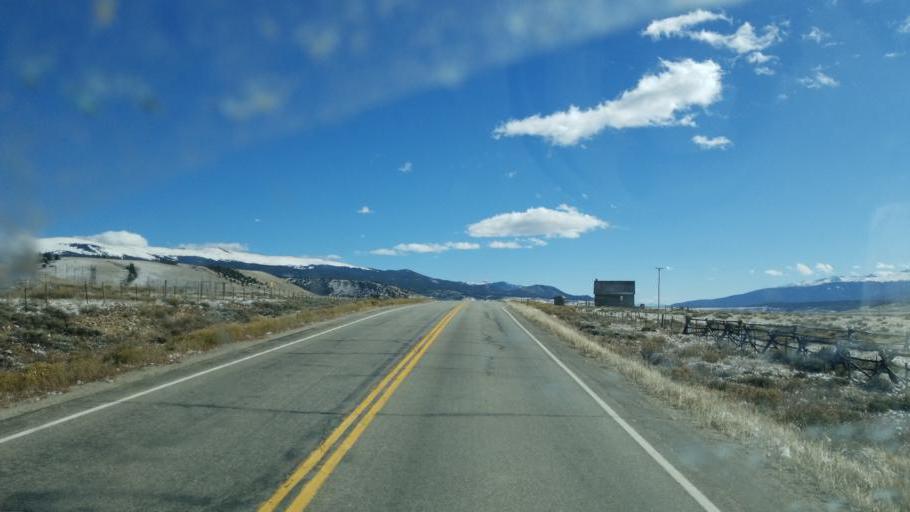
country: US
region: Colorado
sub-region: Lake County
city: Leadville
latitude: 39.1939
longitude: -106.3354
